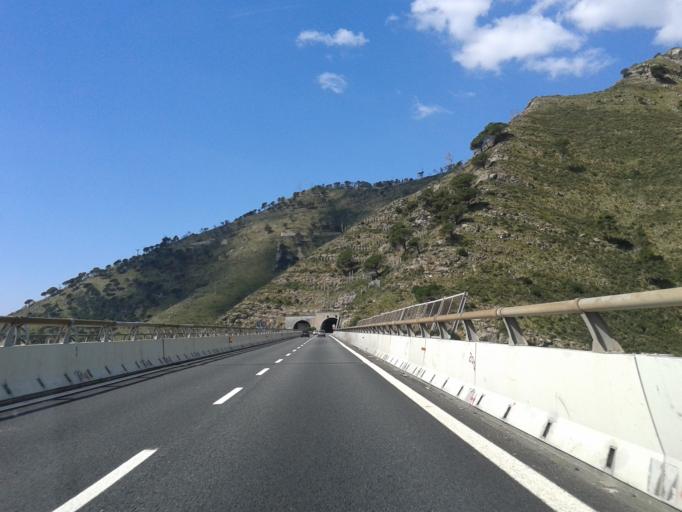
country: IT
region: Liguria
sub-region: Provincia di Genova
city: Bogliasco
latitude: 44.3926
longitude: 9.0418
